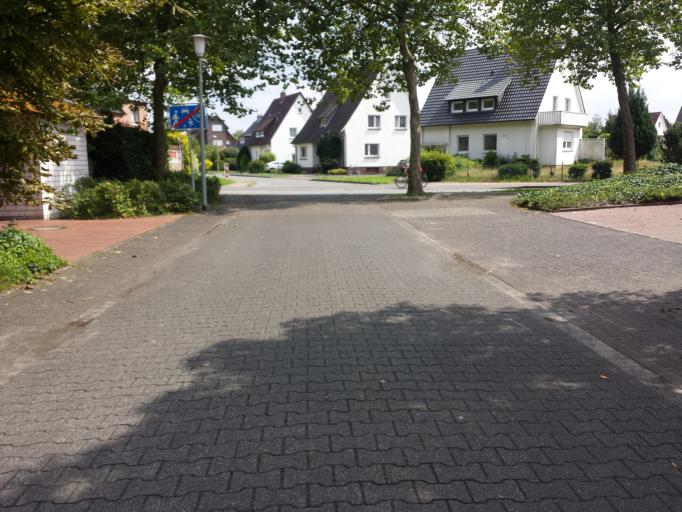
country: DE
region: North Rhine-Westphalia
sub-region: Regierungsbezirk Detmold
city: Guetersloh
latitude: 51.8869
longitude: 8.3827
